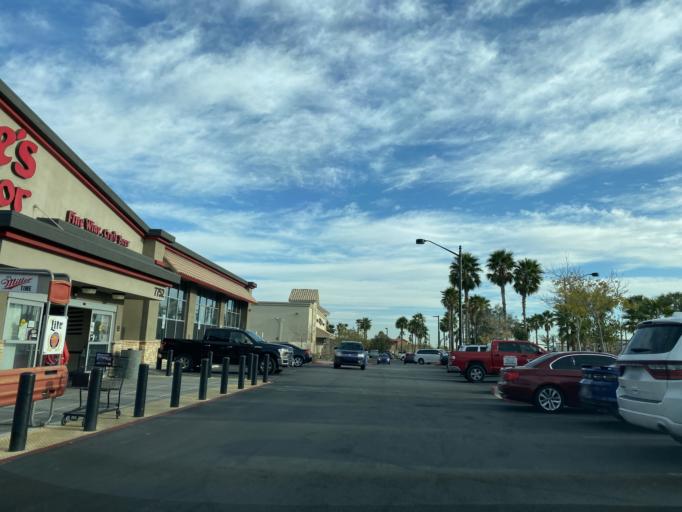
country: US
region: Nevada
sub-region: Clark County
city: Summerlin South
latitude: 36.3024
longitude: -115.2838
